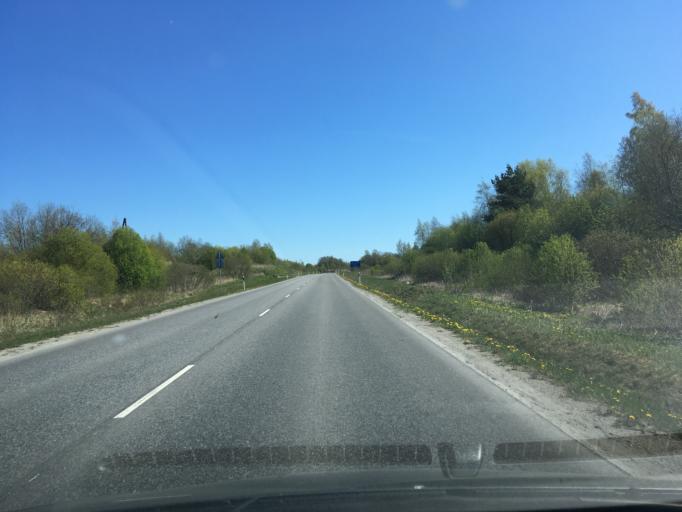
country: EE
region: Harju
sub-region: Maardu linn
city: Maardu
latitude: 59.4540
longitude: 25.0217
